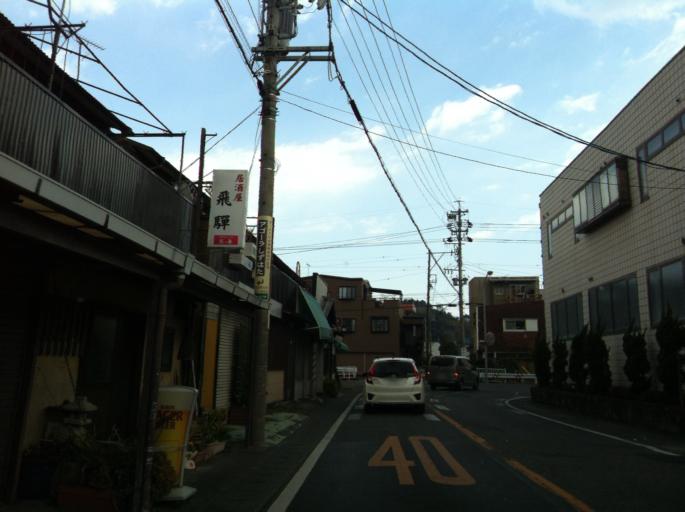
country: JP
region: Shizuoka
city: Shizuoka-shi
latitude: 35.0035
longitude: 138.3642
